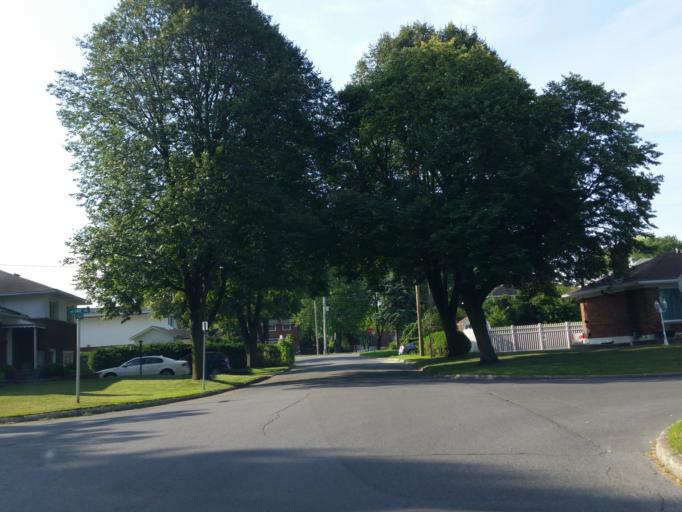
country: CA
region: Ontario
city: Ottawa
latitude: 45.3572
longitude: -75.7521
